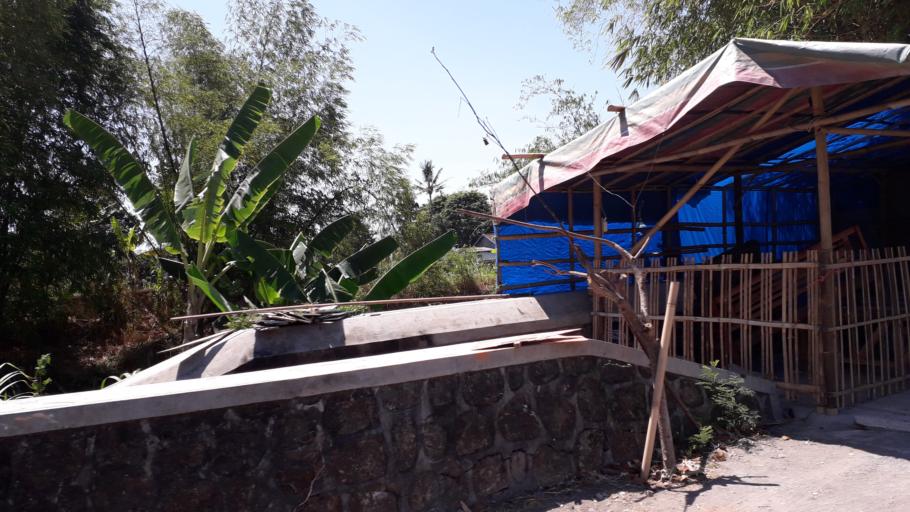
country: ID
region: Daerah Istimewa Yogyakarta
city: Pundong
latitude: -7.9627
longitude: 110.3215
